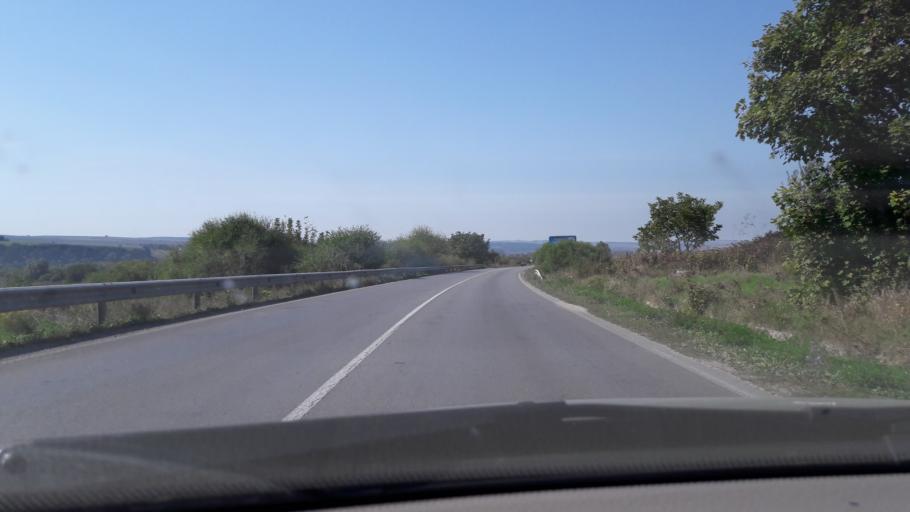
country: BG
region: Razgrad
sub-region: Obshtina Razgrad
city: Razgrad
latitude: 43.5440
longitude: 26.5025
